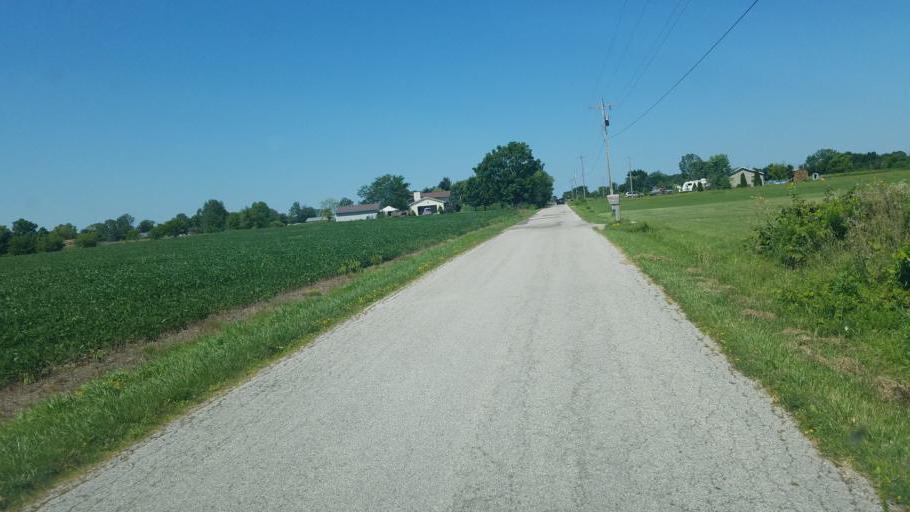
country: US
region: Ohio
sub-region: Delaware County
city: Ashley
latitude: 40.4333
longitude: -83.0066
